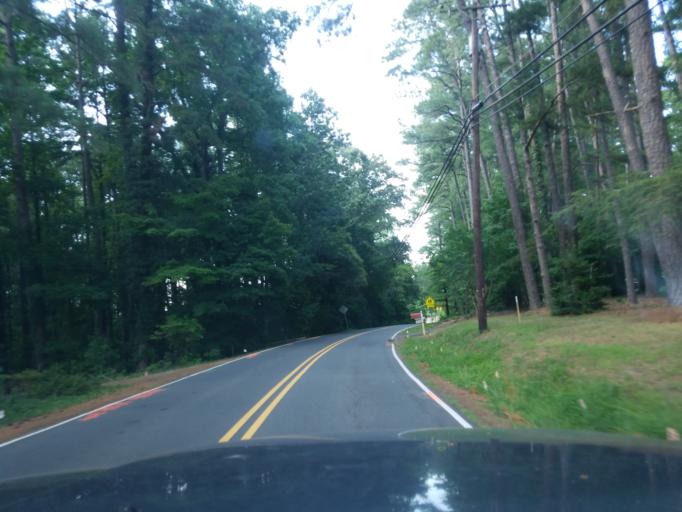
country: US
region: North Carolina
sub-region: Durham County
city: Durham
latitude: 35.9709
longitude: -78.9324
